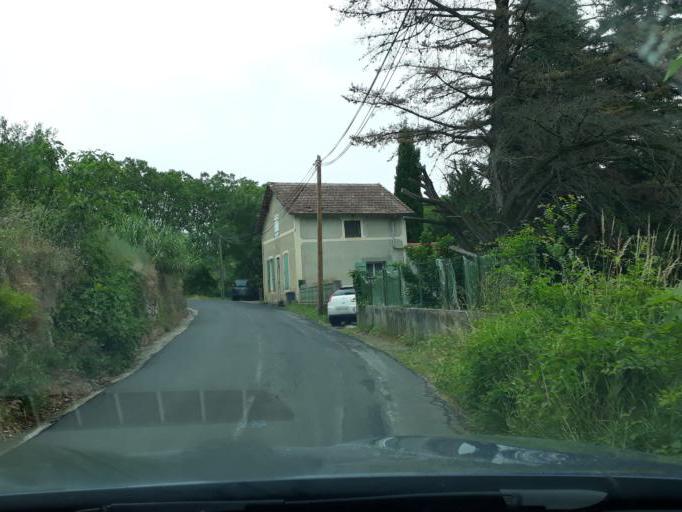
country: FR
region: Languedoc-Roussillon
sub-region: Departement de l'Herault
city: Lodeve
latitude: 43.7608
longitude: 3.3255
